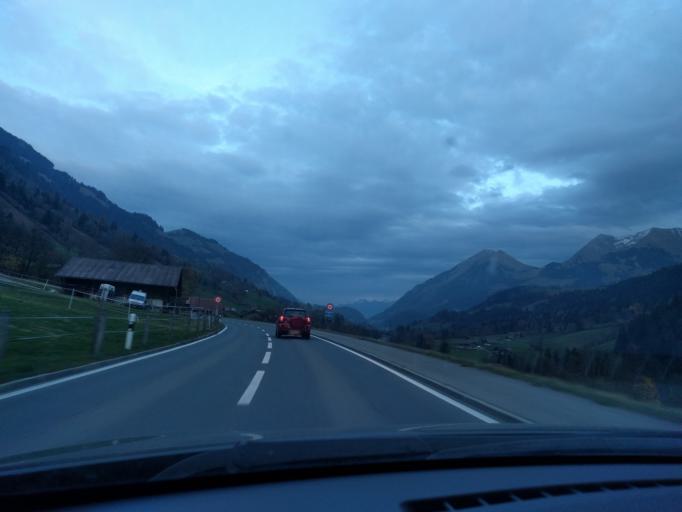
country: CH
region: Bern
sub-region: Frutigen-Niedersimmental District
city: Erlenbach im Simmental
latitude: 46.6578
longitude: 7.5196
